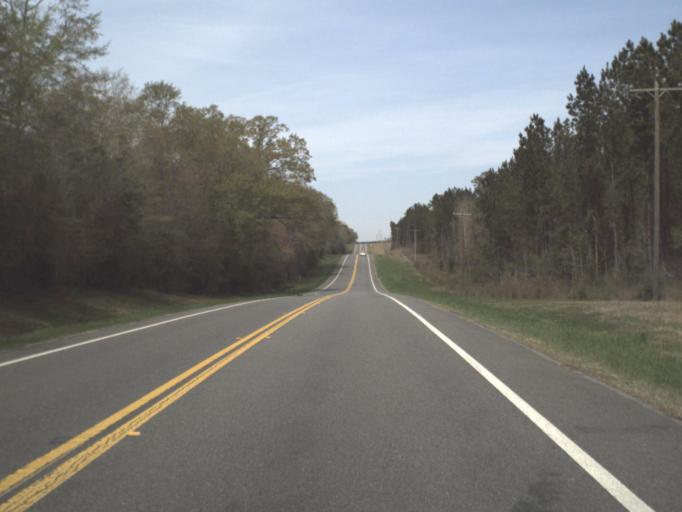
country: US
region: Alabama
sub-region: Geneva County
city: Geneva
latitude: 30.9176
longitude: -85.9607
